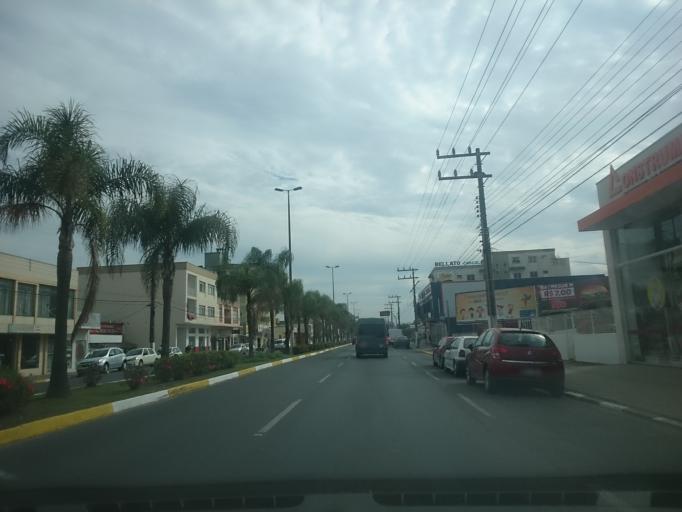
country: BR
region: Santa Catarina
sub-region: Lages
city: Lages
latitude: -27.8017
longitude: -50.3050
